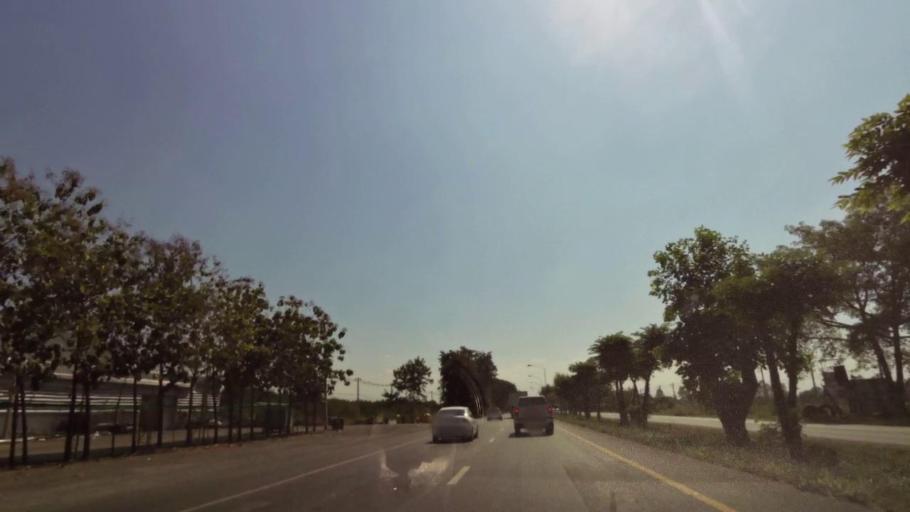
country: TH
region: Nakhon Sawan
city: Kao Liao
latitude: 15.8019
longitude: 100.1202
